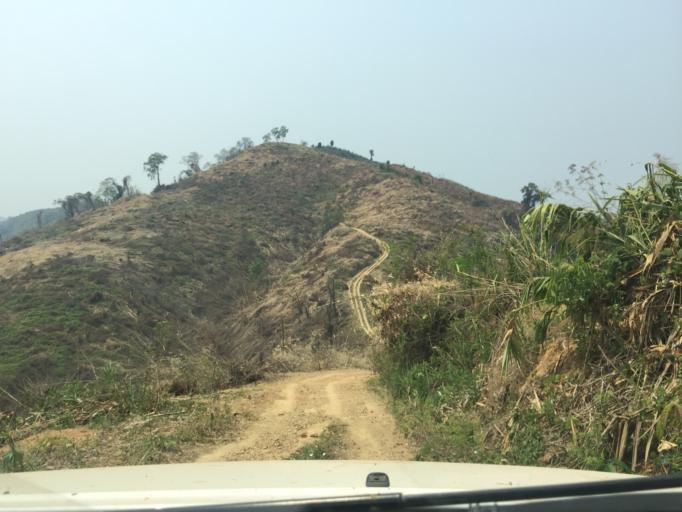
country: LA
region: Loungnamtha
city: Muang Nale
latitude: 20.6204
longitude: 101.6162
